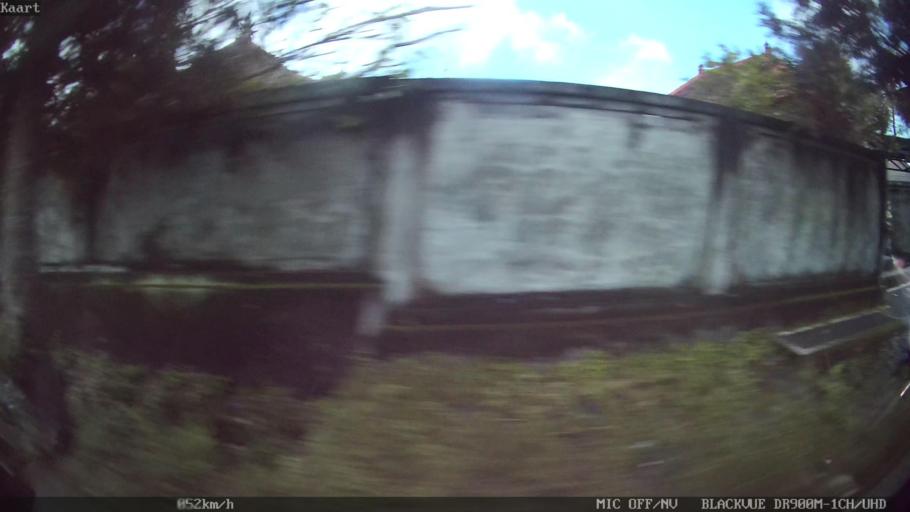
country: ID
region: Bali
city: Banjar Mulung
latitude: -8.5035
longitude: 115.3214
